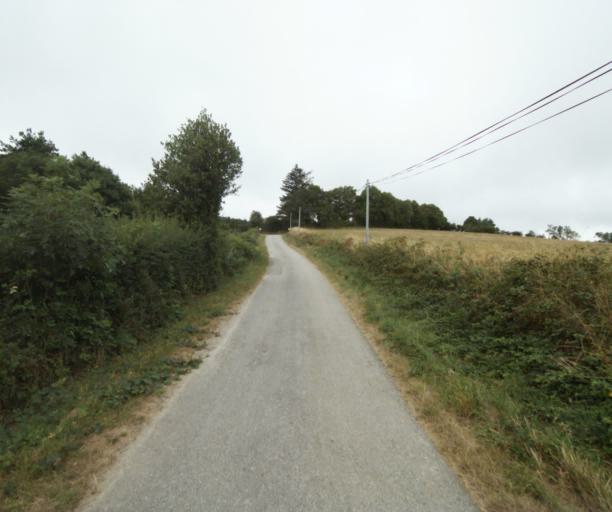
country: FR
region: Midi-Pyrenees
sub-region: Departement du Tarn
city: Soreze
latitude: 43.4127
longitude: 2.0467
